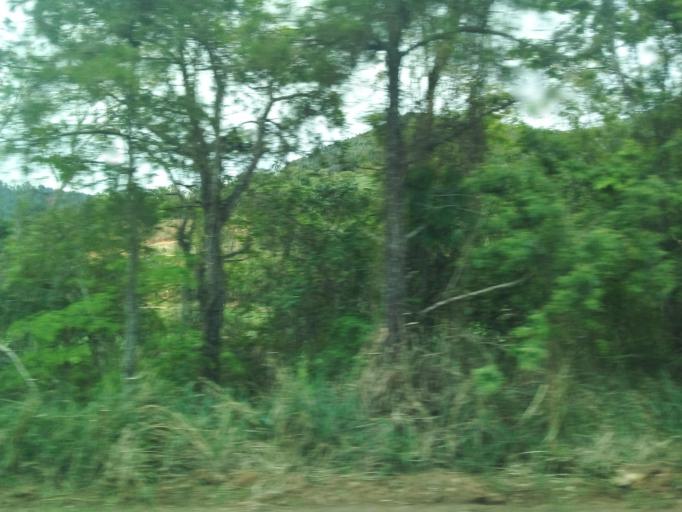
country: BR
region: Minas Gerais
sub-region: Nova Era
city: Nova Era
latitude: -19.7812
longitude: -43.0920
